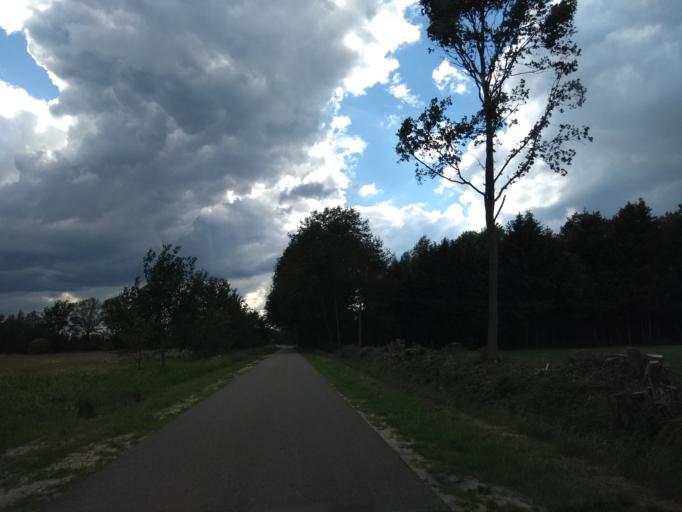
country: DE
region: Lower Saxony
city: Nordhorn
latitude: 52.3698
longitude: 7.0463
